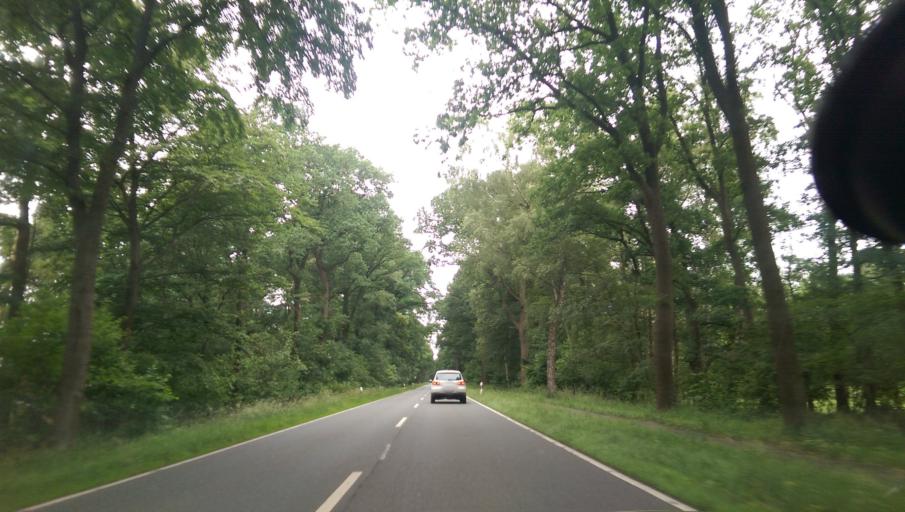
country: DE
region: Lower Saxony
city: Hemsbunde
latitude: 53.0745
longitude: 9.4353
